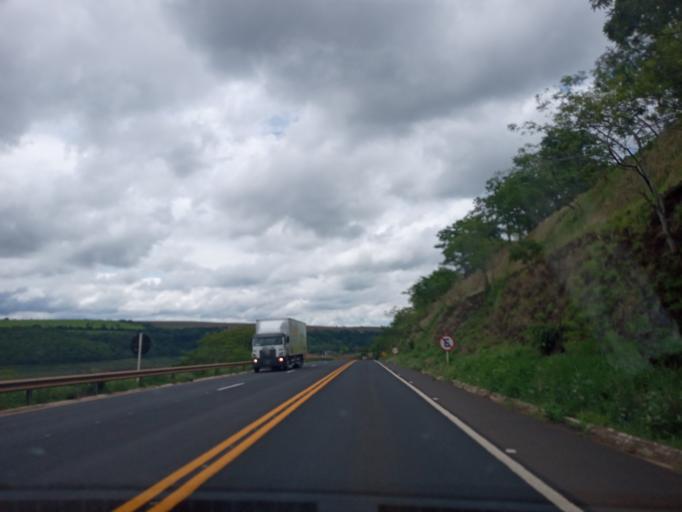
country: BR
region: Minas Gerais
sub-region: Uberaba
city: Uberaba
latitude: -19.2749
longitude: -47.6293
